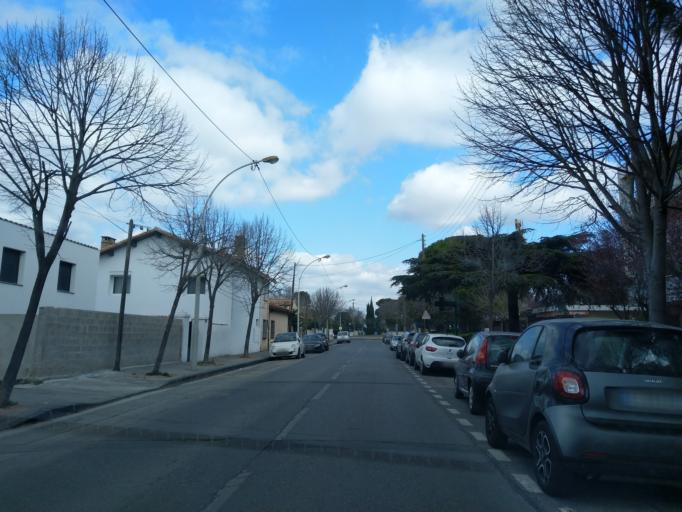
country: FR
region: Provence-Alpes-Cote d'Azur
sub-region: Departement des Bouches-du-Rhone
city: Marseille 12
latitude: 43.3168
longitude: 5.4472
